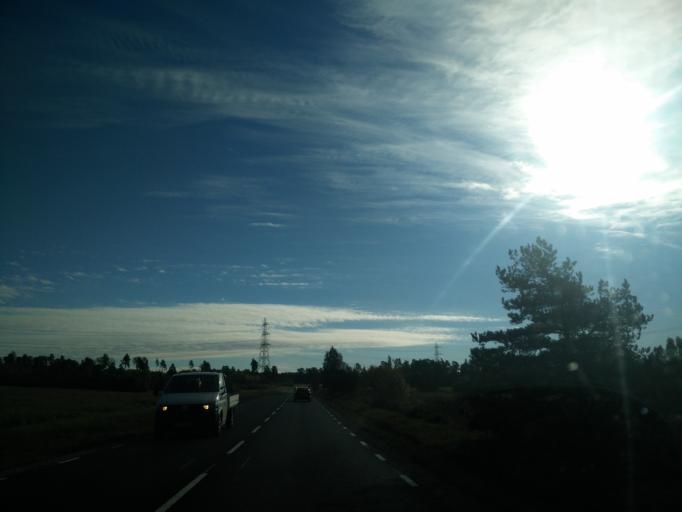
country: SE
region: Stockholm
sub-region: Upplands Vasby Kommun
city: Upplands Vaesby
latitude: 59.5082
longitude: 17.9668
